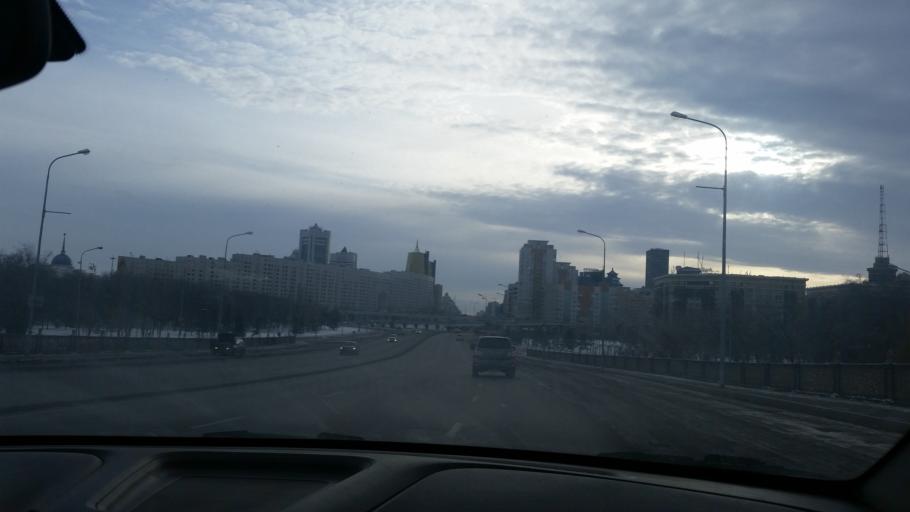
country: KZ
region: Astana Qalasy
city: Astana
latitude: 51.1361
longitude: 71.4418
